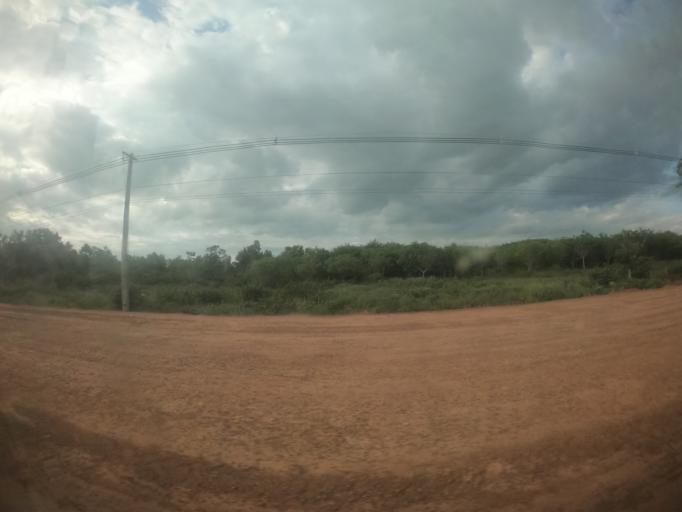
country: TH
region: Surin
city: Kap Choeng
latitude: 14.4689
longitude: 103.6241
